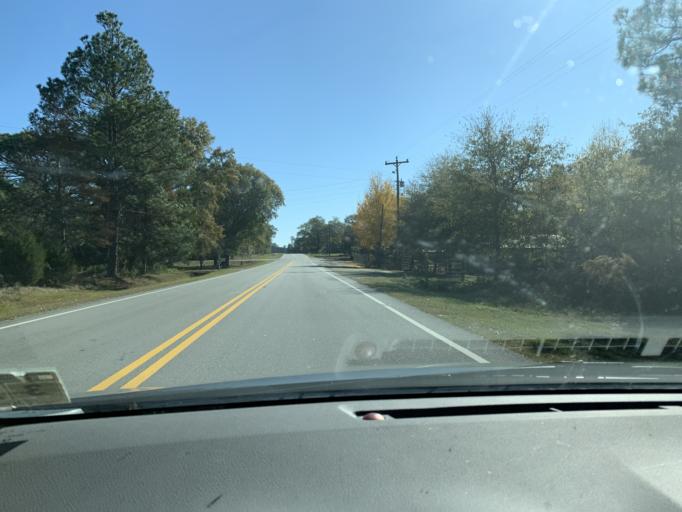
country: US
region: Georgia
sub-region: Ben Hill County
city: Fitzgerald
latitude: 31.7054
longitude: -83.1576
